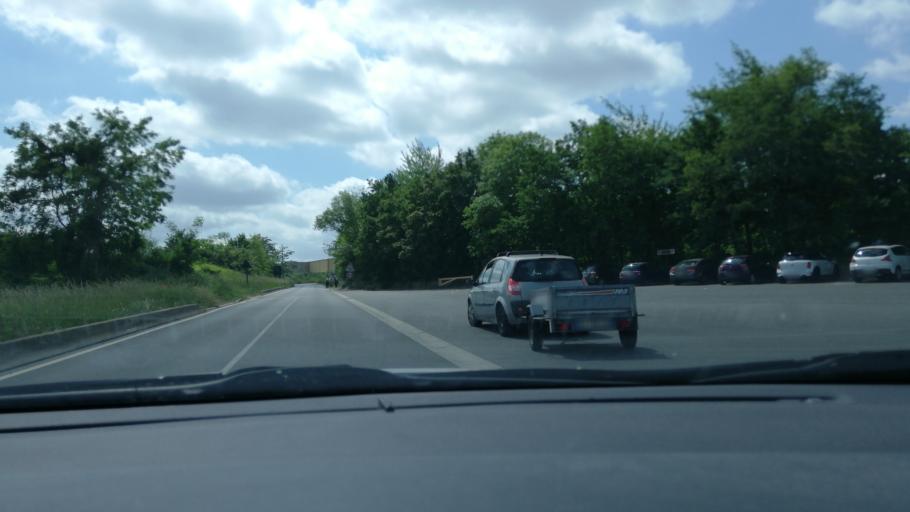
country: FR
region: Ile-de-France
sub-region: Departement du Val-d'Oise
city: Vaureal
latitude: 49.0678
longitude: 2.0242
